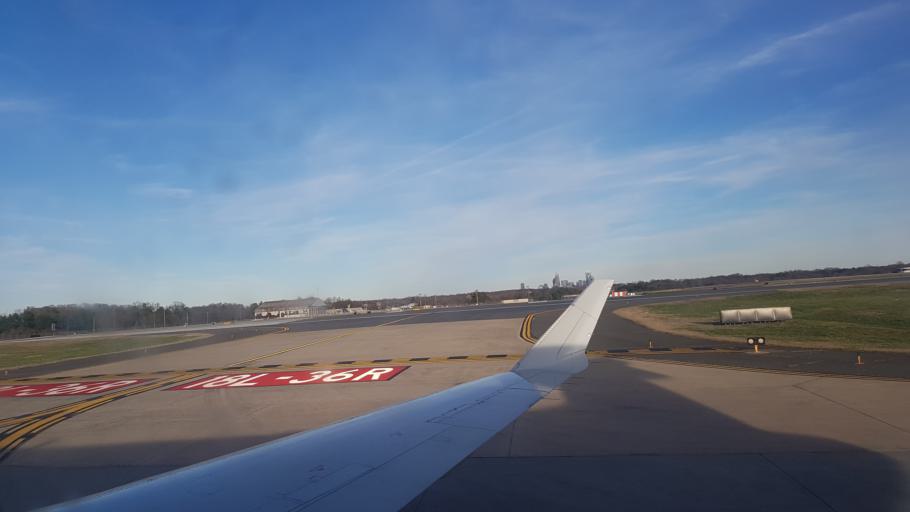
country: US
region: North Carolina
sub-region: Mecklenburg County
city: Charlotte
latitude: 35.2238
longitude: -80.9374
